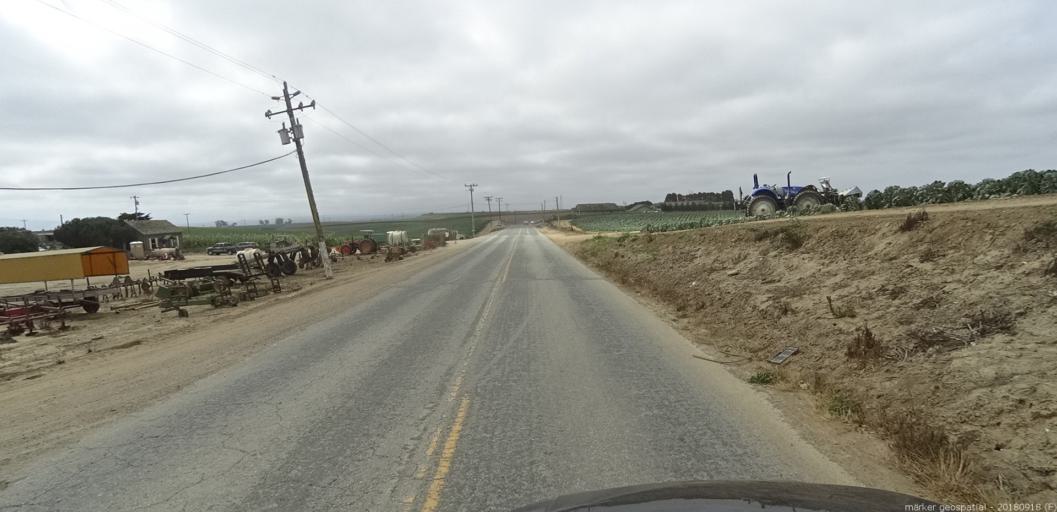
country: US
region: California
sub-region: Monterey County
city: Castroville
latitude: 36.7686
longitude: -121.7235
